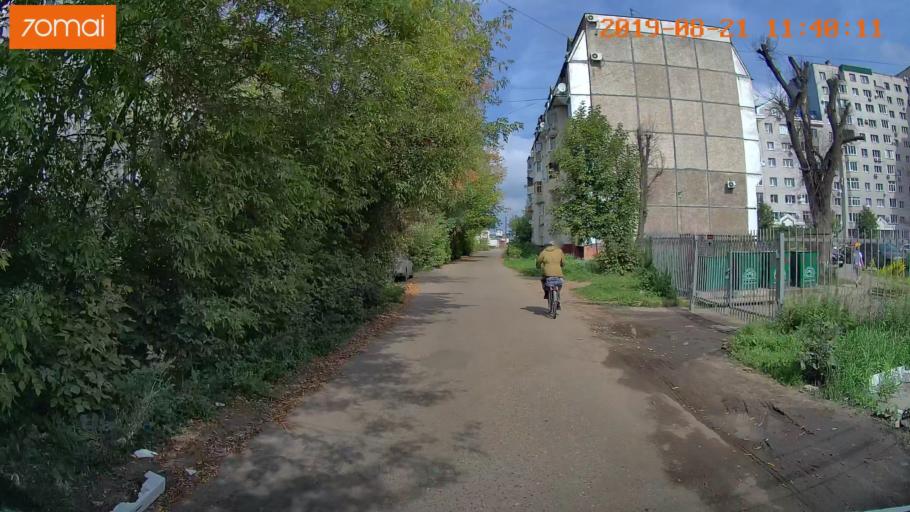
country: RU
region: Ivanovo
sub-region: Gorod Ivanovo
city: Ivanovo
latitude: 57.0021
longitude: 40.9377
